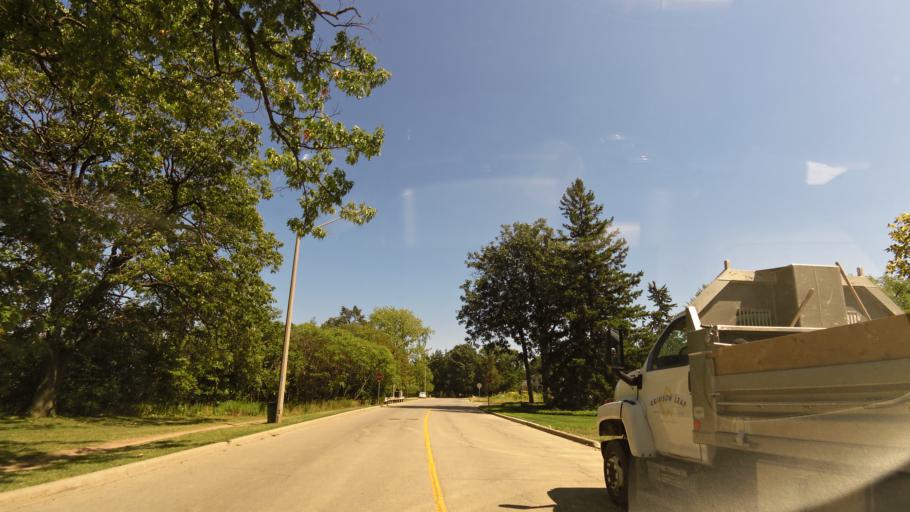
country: CA
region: Ontario
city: Ancaster
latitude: 43.2456
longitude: -79.9234
